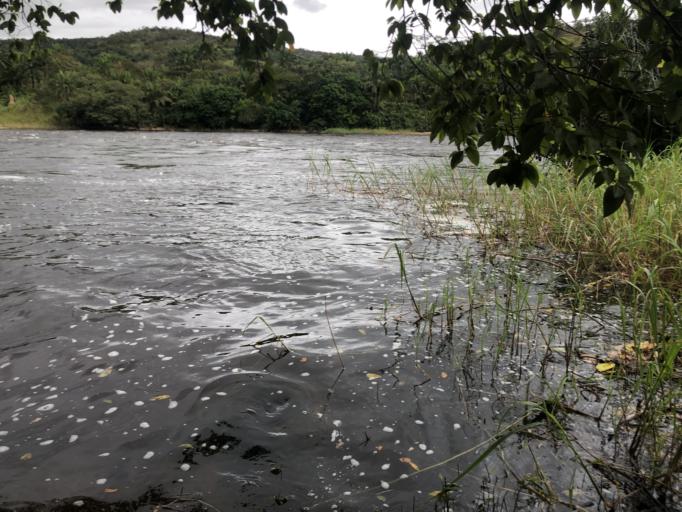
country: CD
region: Bandundu
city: Kikwit
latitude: -5.5414
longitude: 19.2340
